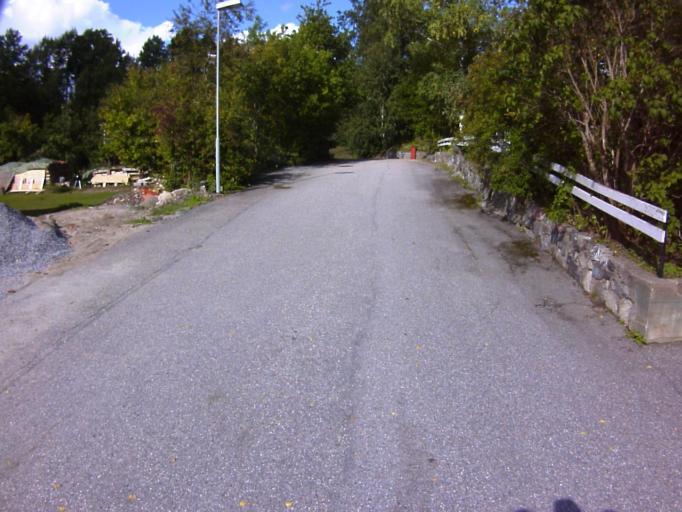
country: SE
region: Soedermanland
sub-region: Eskilstuna Kommun
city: Eskilstuna
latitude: 59.3964
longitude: 16.5366
